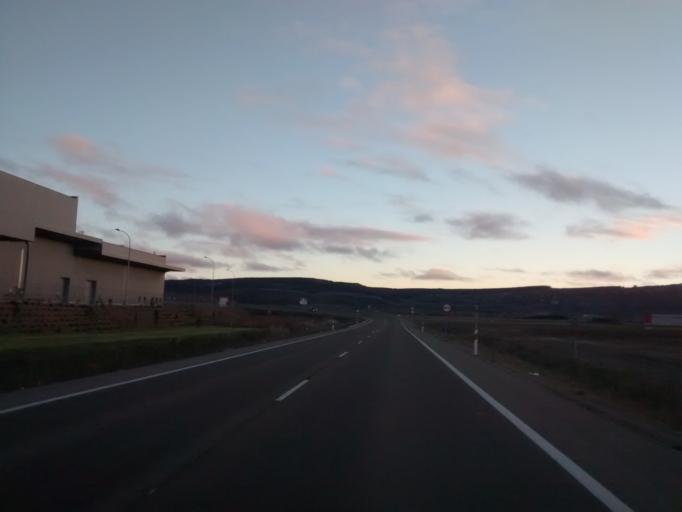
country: ES
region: Castille and Leon
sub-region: Provincia de Palencia
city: Aguilar de Campoo
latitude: 42.7845
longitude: -4.2446
